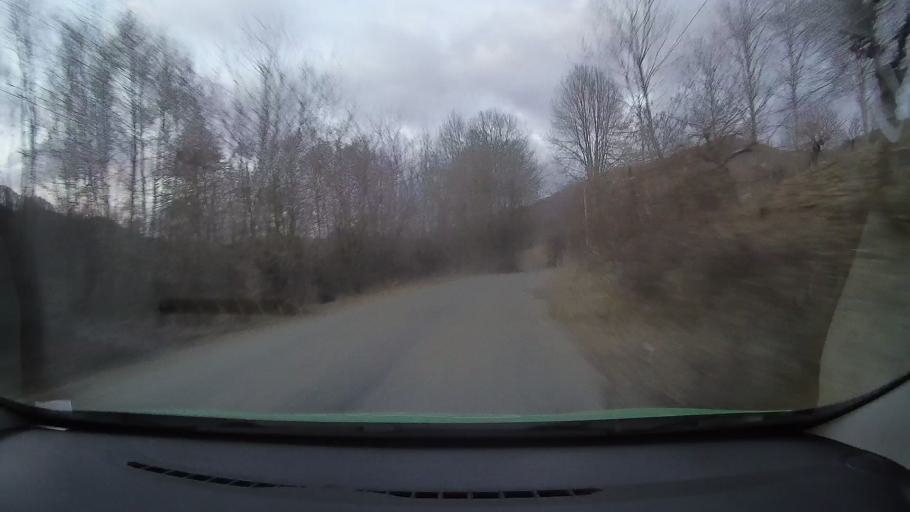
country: RO
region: Dambovita
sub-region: Comuna Valea Lunga
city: Valea Lunga-Cricov
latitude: 45.0871
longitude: 25.5799
